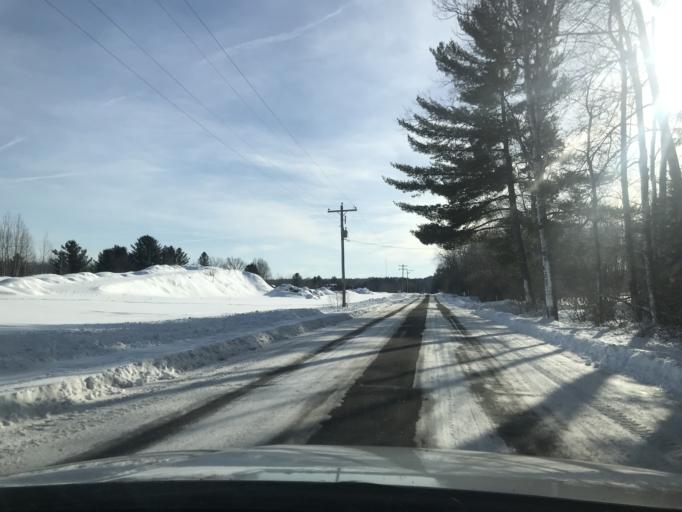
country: US
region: Wisconsin
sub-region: Menominee County
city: Legend Lake
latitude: 45.3113
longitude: -88.5218
